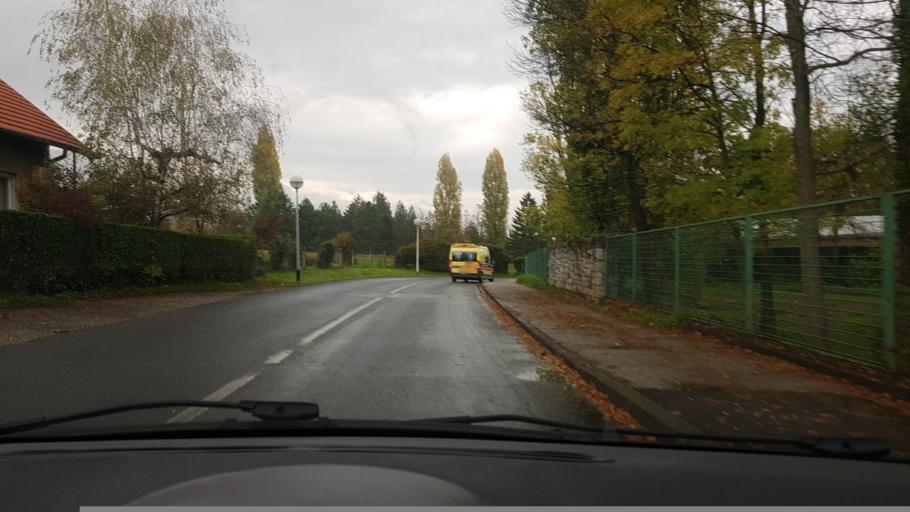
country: HR
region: Grad Zagreb
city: Zagreb
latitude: 45.8310
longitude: 15.9867
